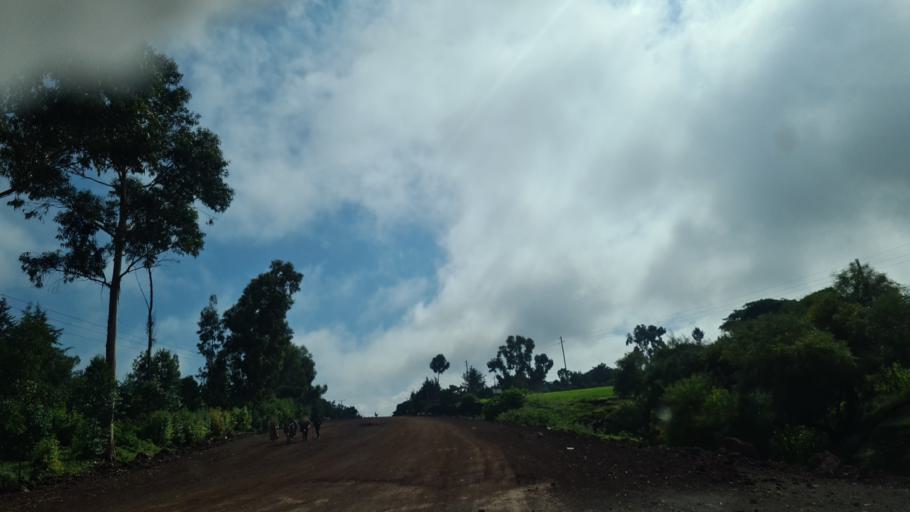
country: ET
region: Oromiya
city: Huruta
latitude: 8.1281
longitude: 39.3790
